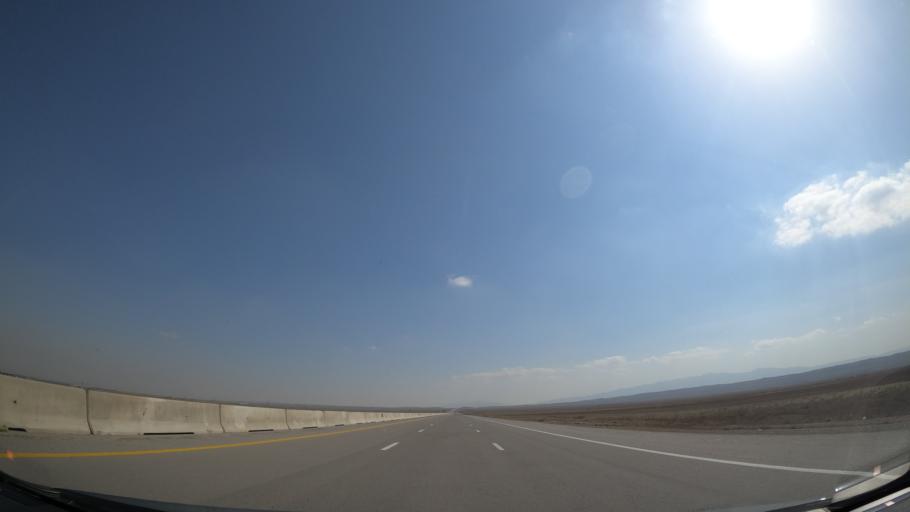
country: IR
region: Alborz
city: Nazarabad
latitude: 35.8342
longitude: 50.4957
